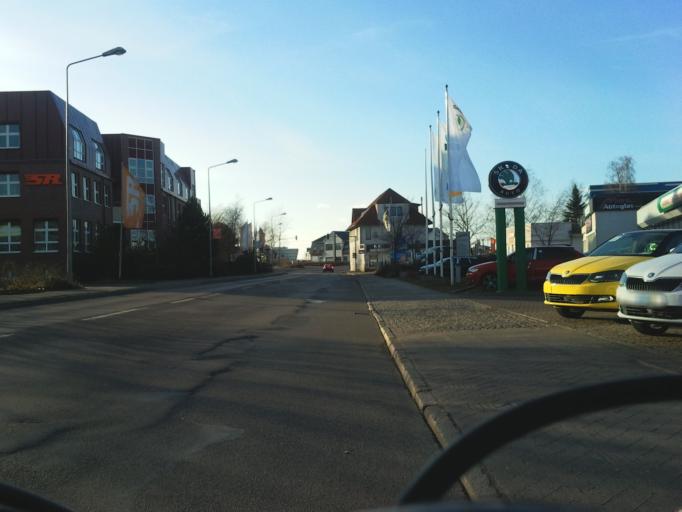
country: DE
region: Mecklenburg-Vorpommern
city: Dierkow-Neu
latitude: 54.0918
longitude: 12.1589
